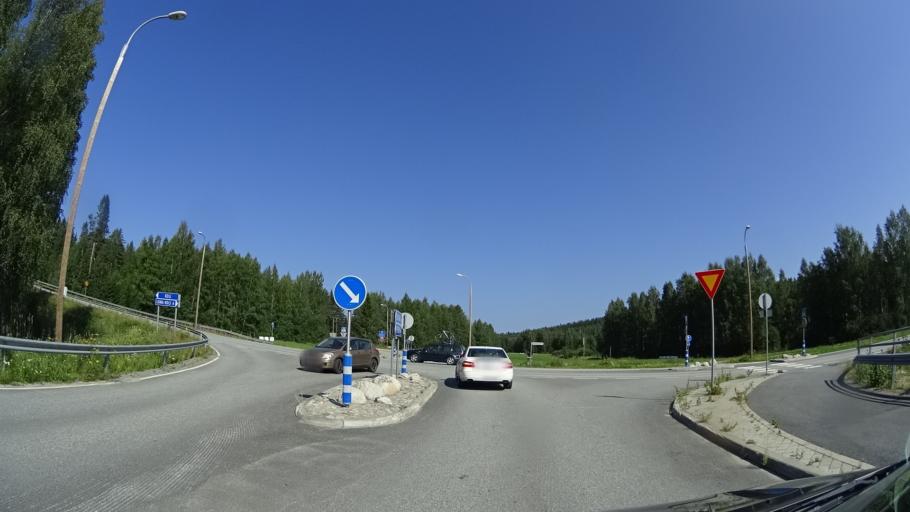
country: FI
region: North Karelia
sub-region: Pielisen Karjala
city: Lieksa
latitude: 63.1192
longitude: 29.7946
